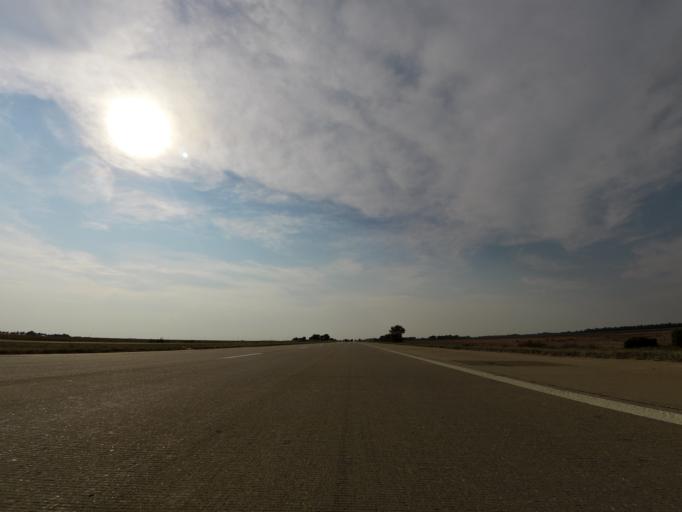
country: US
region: Kansas
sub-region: Sedgwick County
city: Colwich
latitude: 37.8437
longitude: -97.5815
